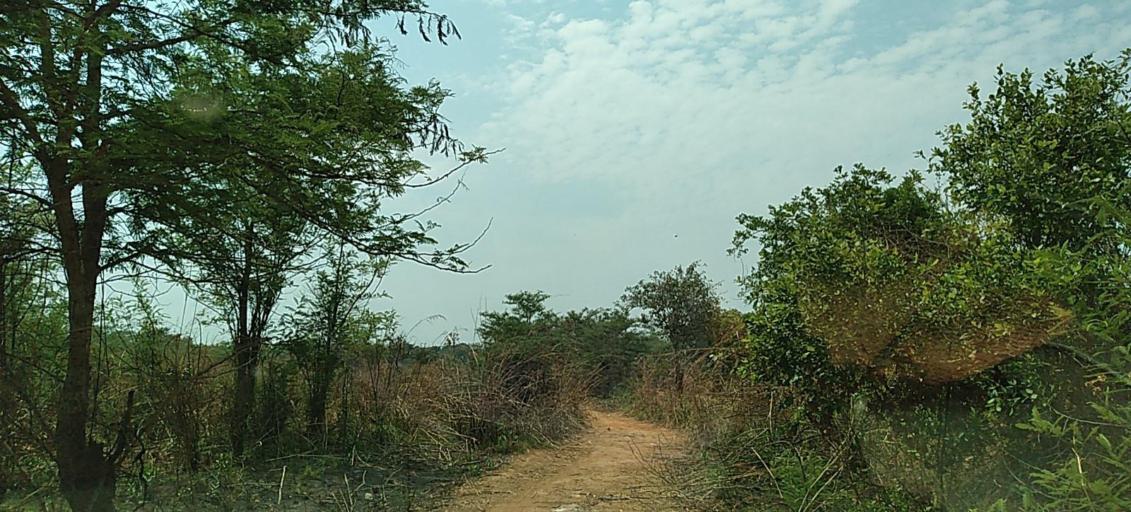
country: ZM
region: Copperbelt
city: Kalulushi
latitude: -12.8942
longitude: 28.0812
